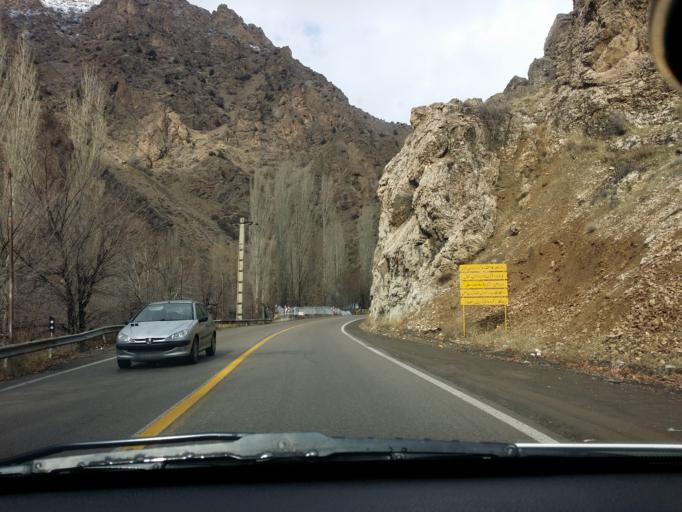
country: IR
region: Tehran
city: Tajrish
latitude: 36.0433
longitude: 51.3112
